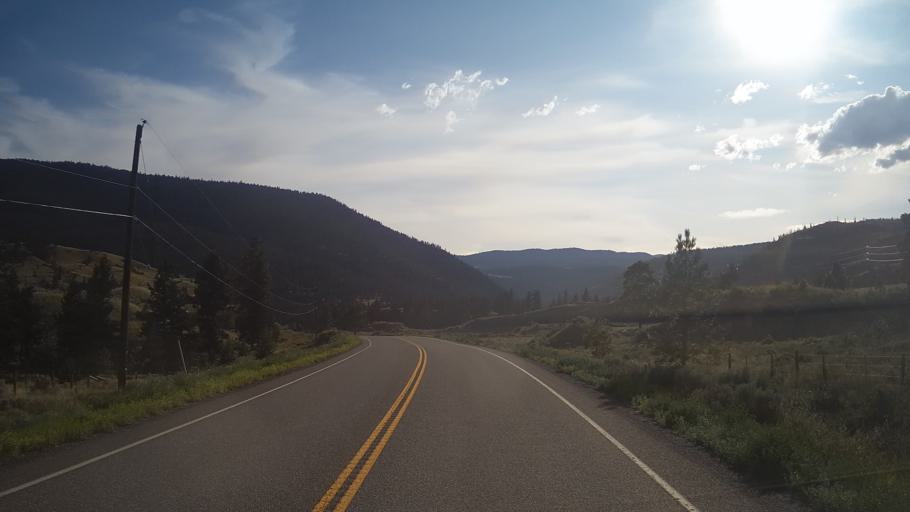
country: CA
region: British Columbia
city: Cache Creek
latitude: 50.8869
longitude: -121.4667
